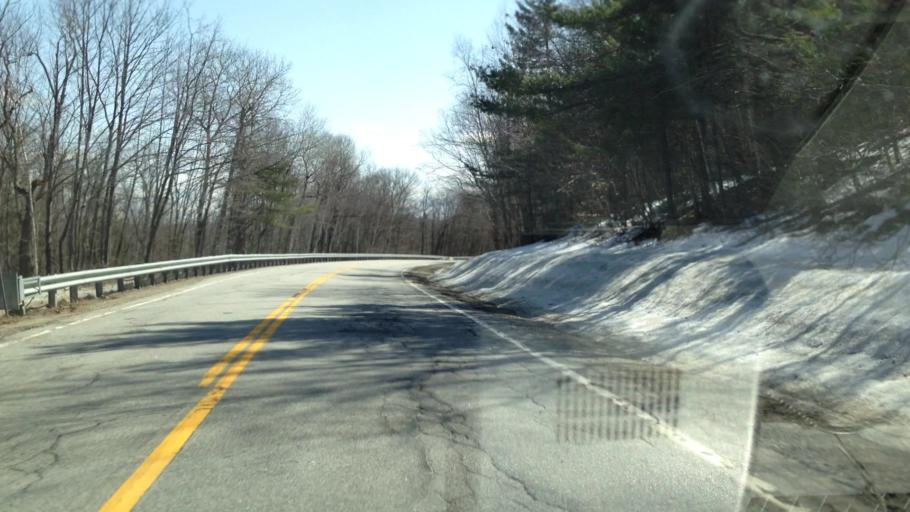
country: US
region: New Hampshire
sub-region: Sullivan County
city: Springfield
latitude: 43.4903
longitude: -71.9824
